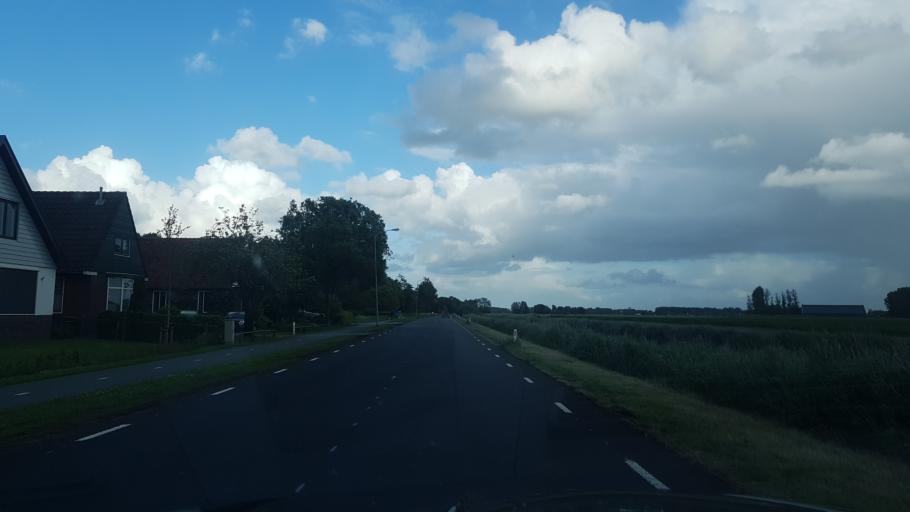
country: NL
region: Groningen
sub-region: Gemeente Appingedam
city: Appingedam
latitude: 53.3258
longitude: 6.7538
